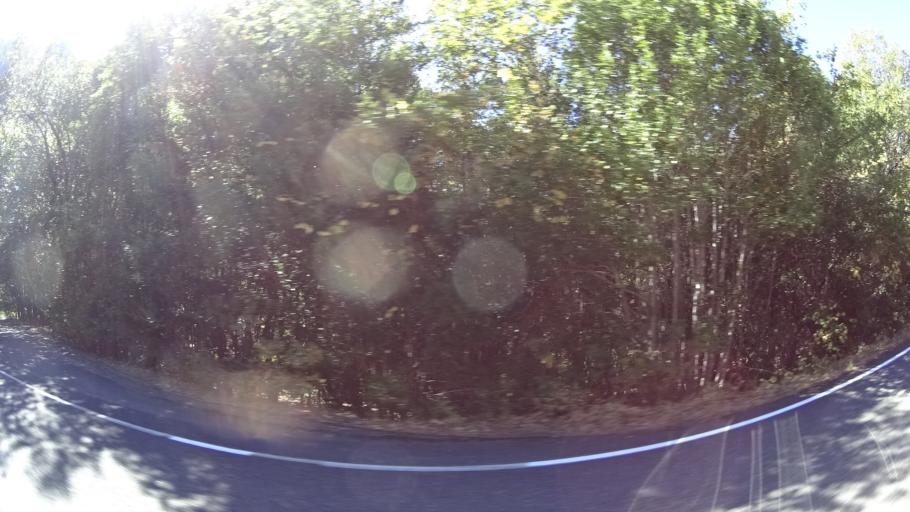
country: US
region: California
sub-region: Siskiyou County
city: Happy Camp
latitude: 41.3793
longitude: -123.4828
